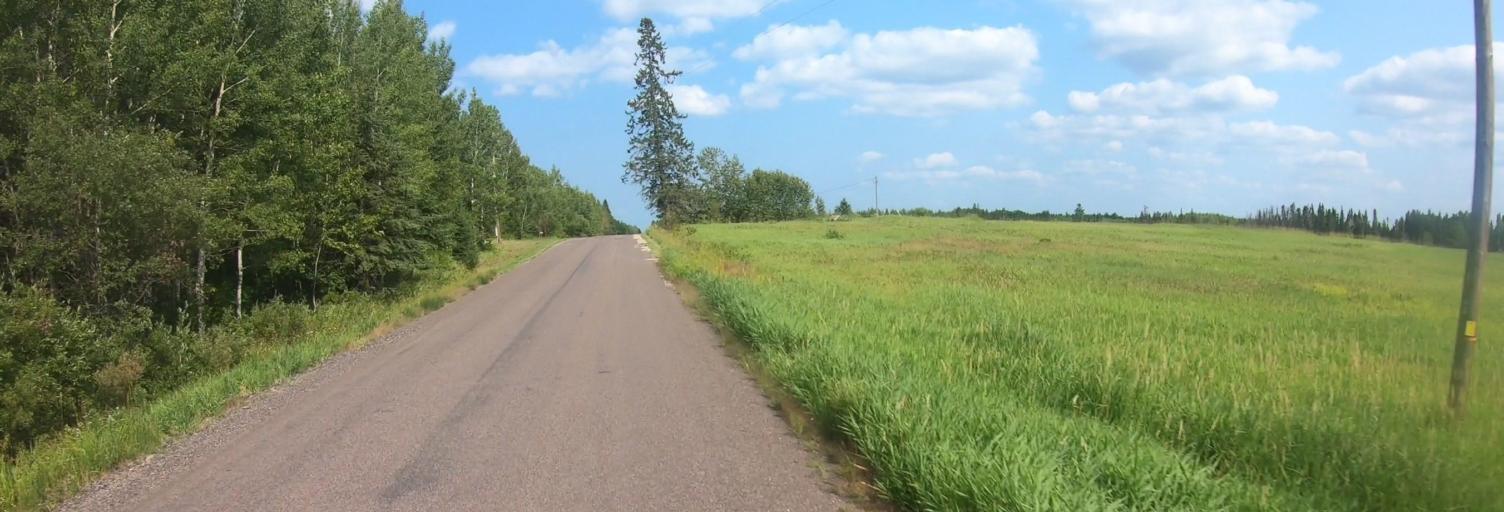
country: US
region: Minnesota
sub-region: Saint Louis County
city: Mountain Iron
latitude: 47.8920
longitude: -92.7079
